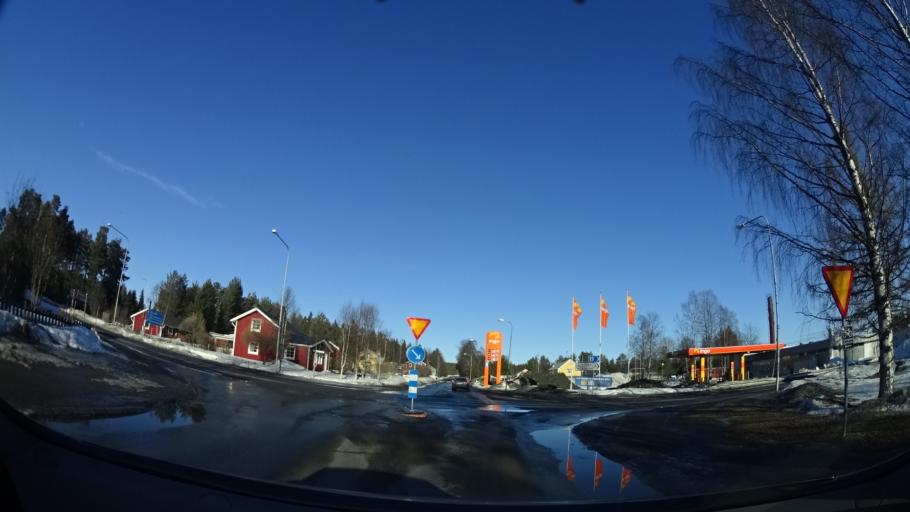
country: SE
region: Vaesterbotten
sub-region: Skelleftea Kommun
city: Byske
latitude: 64.9564
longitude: 21.2085
